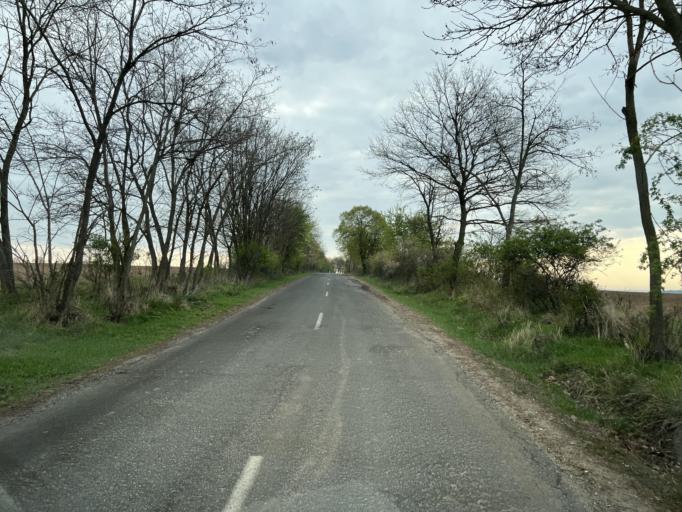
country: HU
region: Pest
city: Acsa
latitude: 47.7896
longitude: 19.4072
